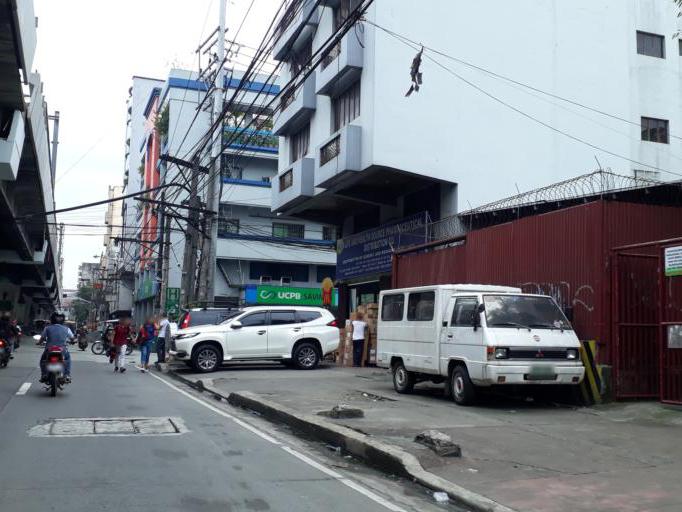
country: PH
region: Metro Manila
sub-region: City of Manila
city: Manila
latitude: 14.6091
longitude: 120.9824
